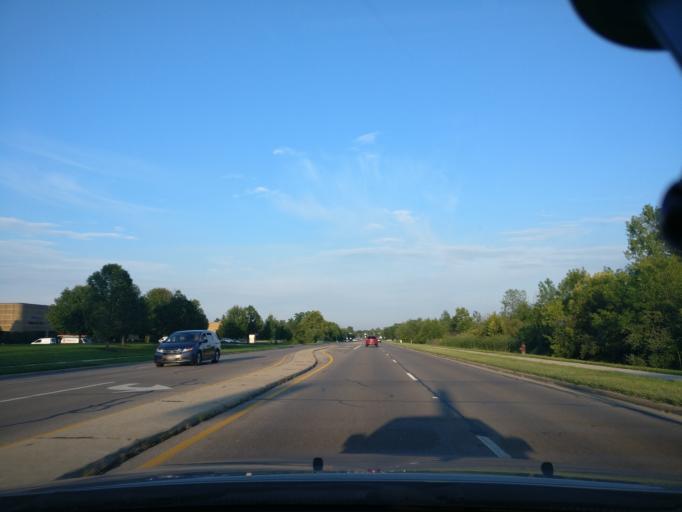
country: US
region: Ohio
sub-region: Montgomery County
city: Centerville
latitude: 39.6269
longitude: -84.2119
